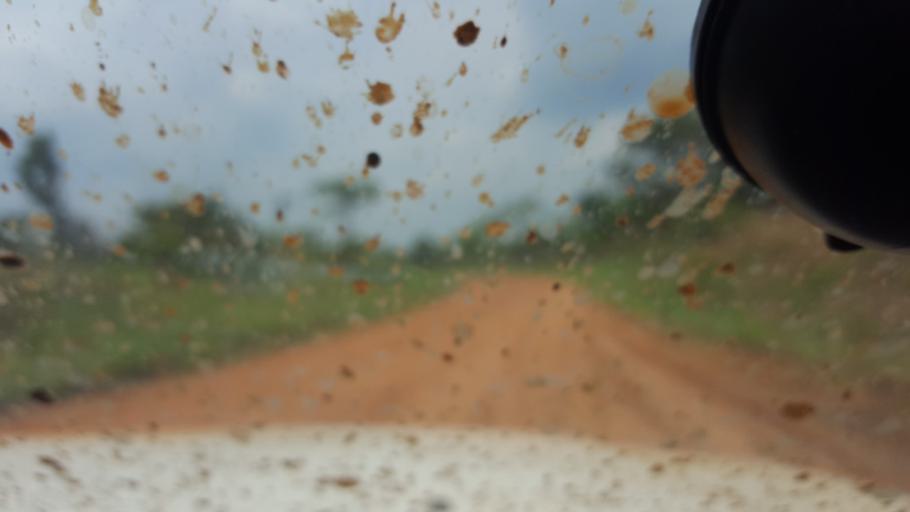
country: CD
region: Bandundu
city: Bandundu
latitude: -3.7621
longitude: 17.1497
